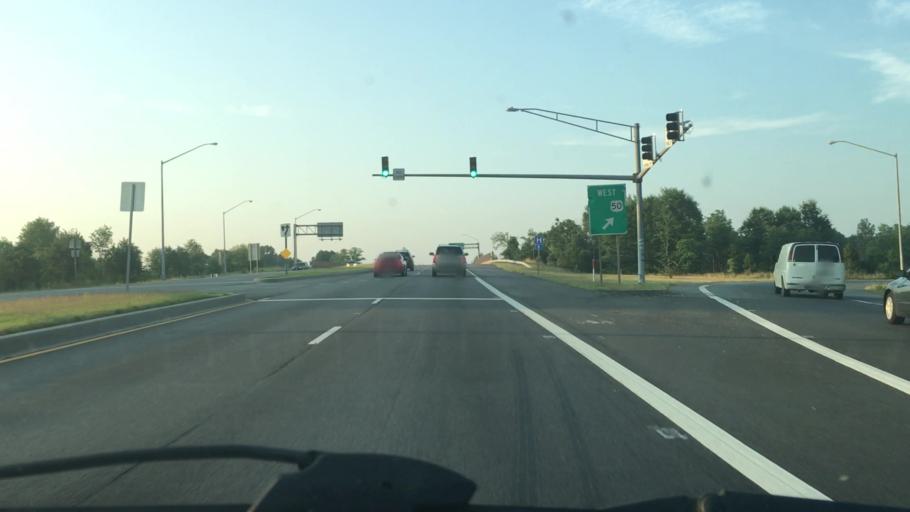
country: US
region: Maryland
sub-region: Prince George's County
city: Bowie
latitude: 38.9549
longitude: -76.7444
